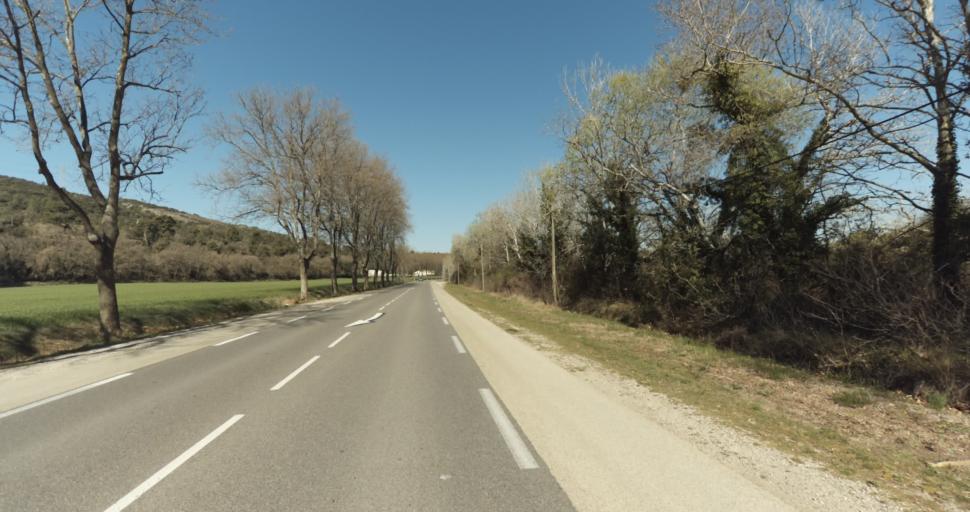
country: FR
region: Provence-Alpes-Cote d'Azur
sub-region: Departement du Vaucluse
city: Cadenet
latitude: 43.6968
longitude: 5.3827
